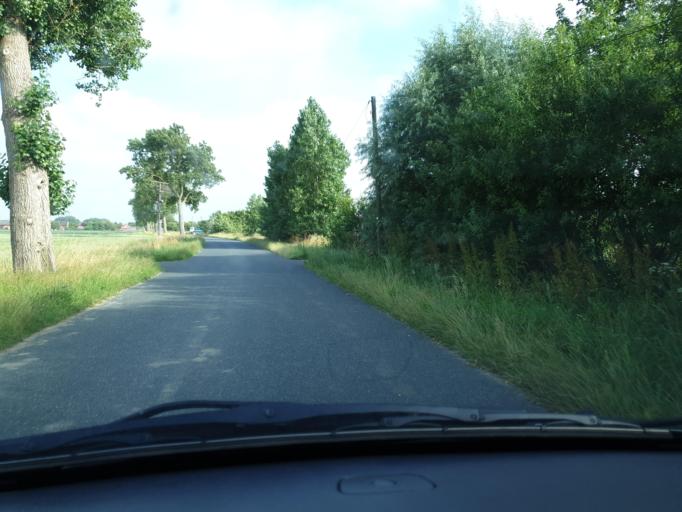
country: DE
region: Schleswig-Holstein
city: Friedrichskoog
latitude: 54.0094
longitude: 8.8668
